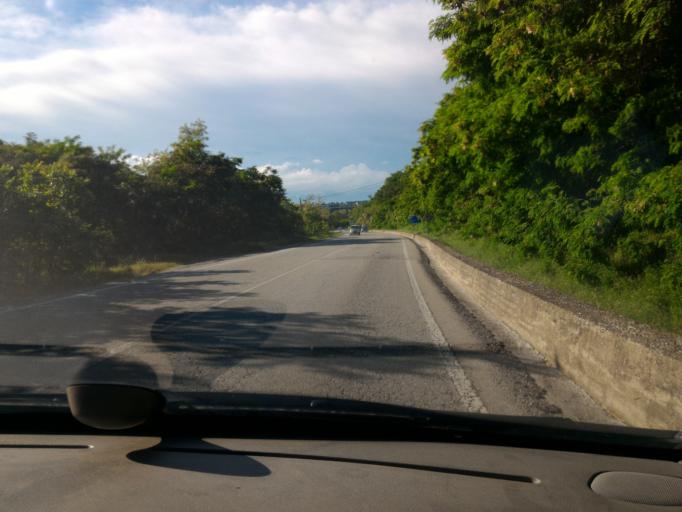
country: IT
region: Piedmont
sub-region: Provincia di Cuneo
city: Sant'Albano Stura
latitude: 44.5130
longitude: 7.7235
